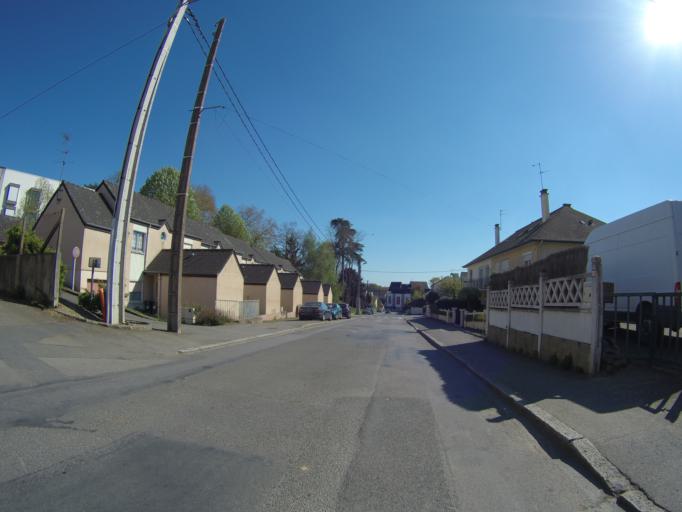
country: FR
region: Brittany
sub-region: Departement d'Ille-et-Vilaine
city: Vern-sur-Seiche
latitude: 48.0479
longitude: -1.6053
